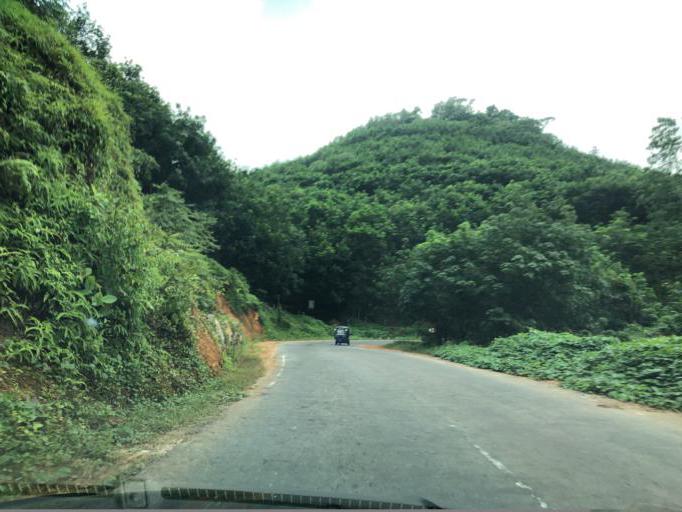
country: LK
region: Western
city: Horana South
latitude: 6.6766
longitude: 80.1254
